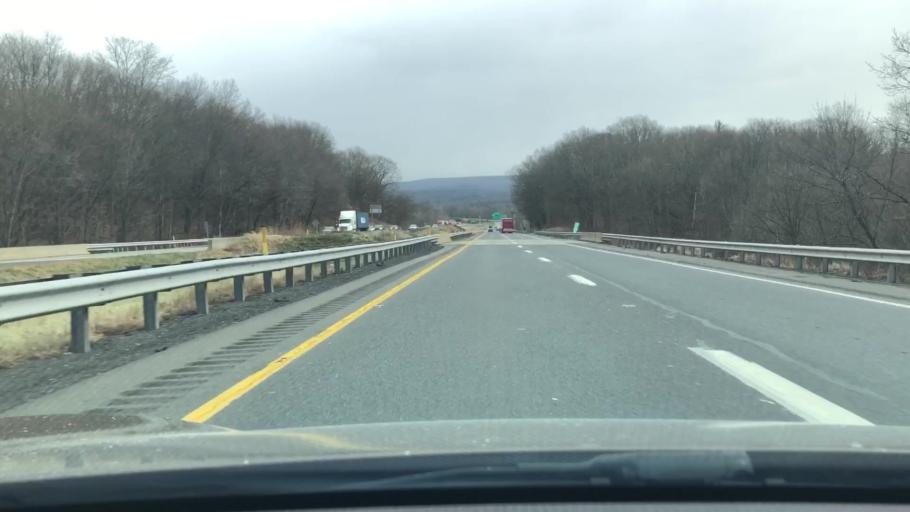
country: US
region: Pennsylvania
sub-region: Monroe County
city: Arlington Heights
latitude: 40.9895
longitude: -75.2441
